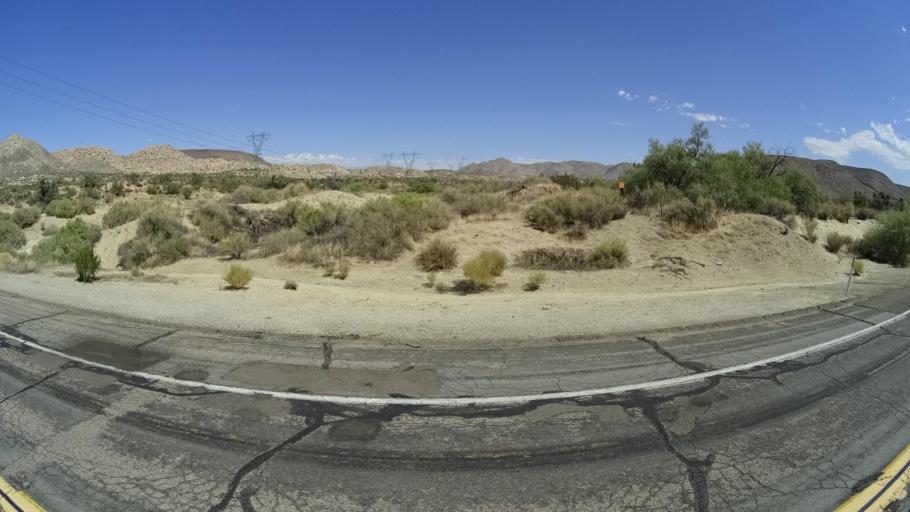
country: MX
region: Baja California
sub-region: Tecate
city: Cereso del Hongo
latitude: 32.6287
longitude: -116.1630
